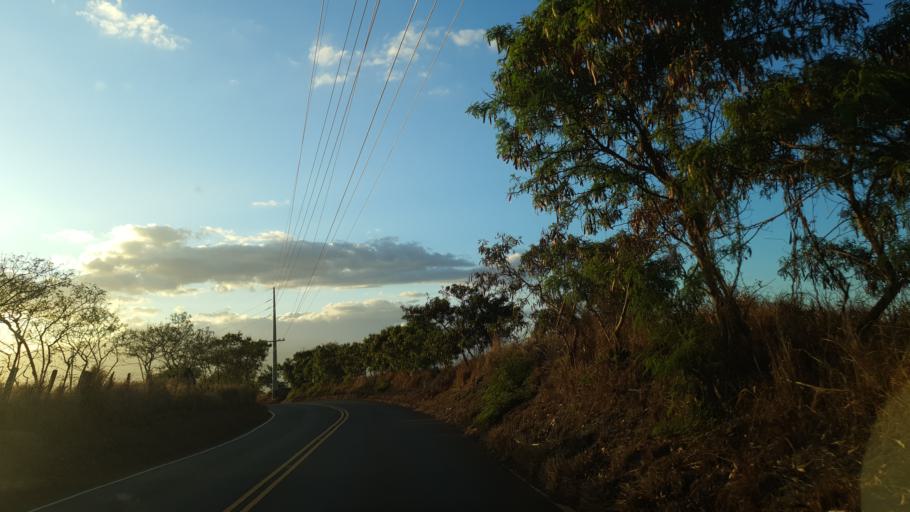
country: US
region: Hawaii
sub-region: Maui County
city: Pukalani
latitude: 20.7911
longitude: -156.3573
